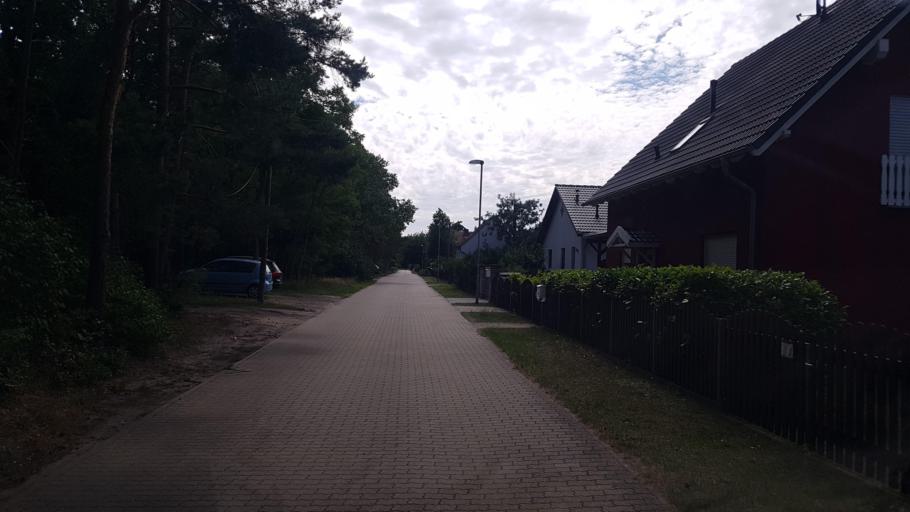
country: DE
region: Brandenburg
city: Luckenwalde
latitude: 52.1145
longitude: 13.1897
